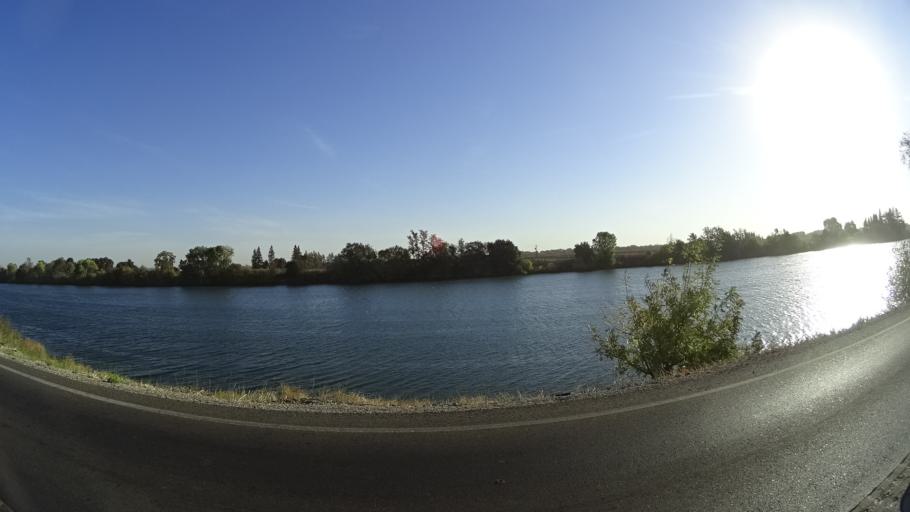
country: US
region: California
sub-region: Sacramento County
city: Laguna
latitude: 38.4075
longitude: -121.5182
